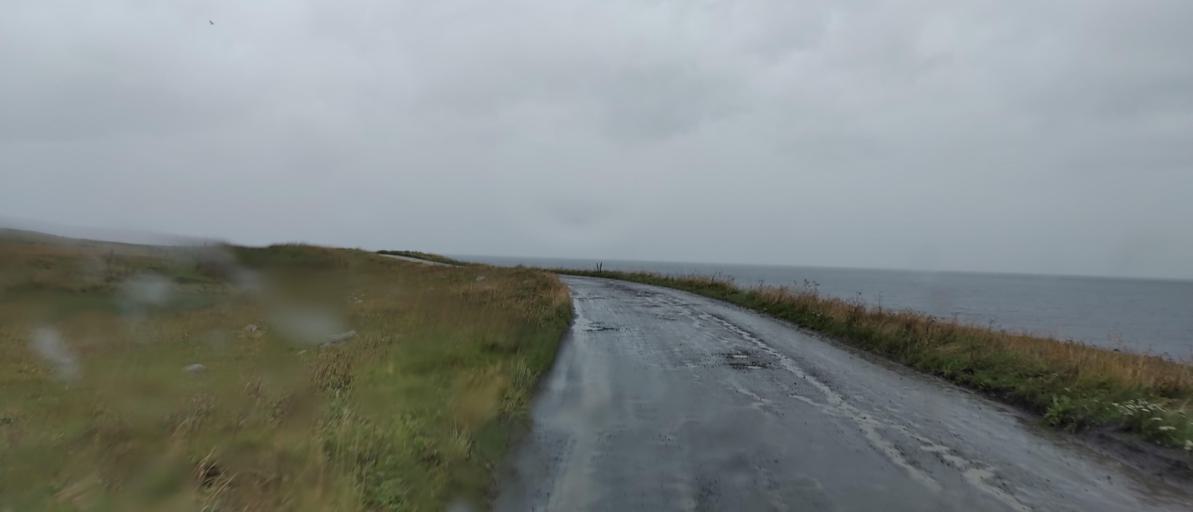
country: NO
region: Nordland
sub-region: Vestvagoy
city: Evjen
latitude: 68.3098
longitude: 13.6607
